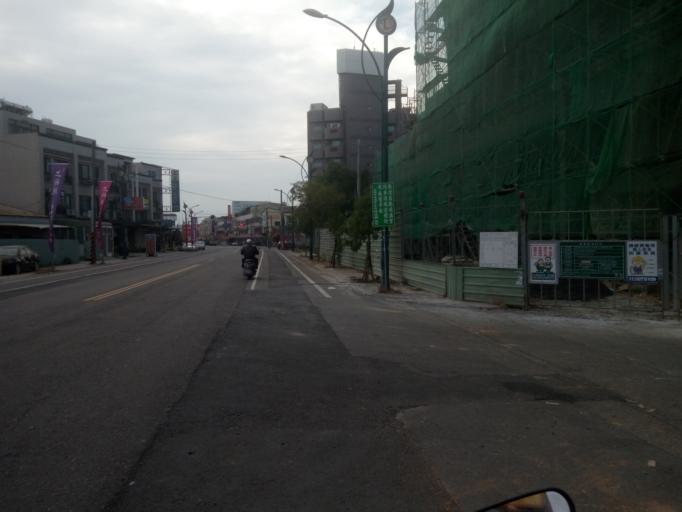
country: TW
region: Taiwan
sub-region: Chiayi
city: Taibao
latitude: 23.4982
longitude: 120.3646
